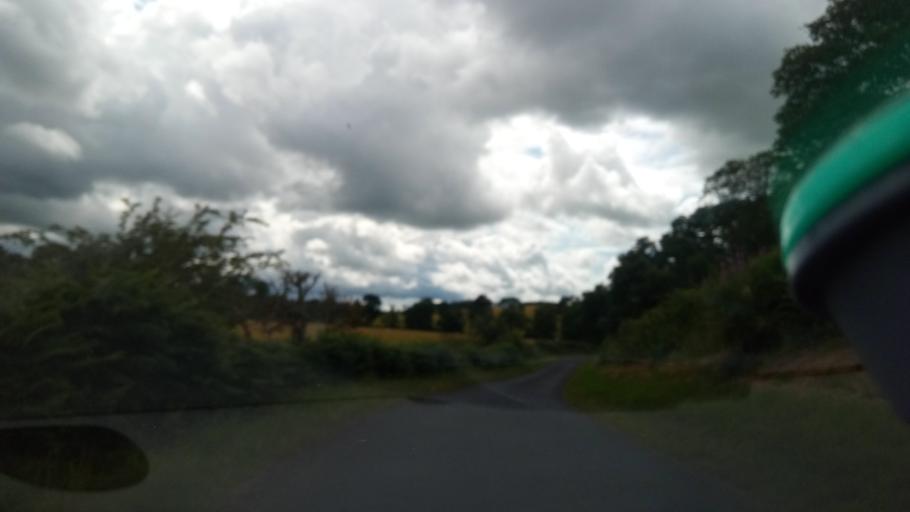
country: GB
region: Scotland
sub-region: The Scottish Borders
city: Kelso
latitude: 55.4880
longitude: -2.4306
